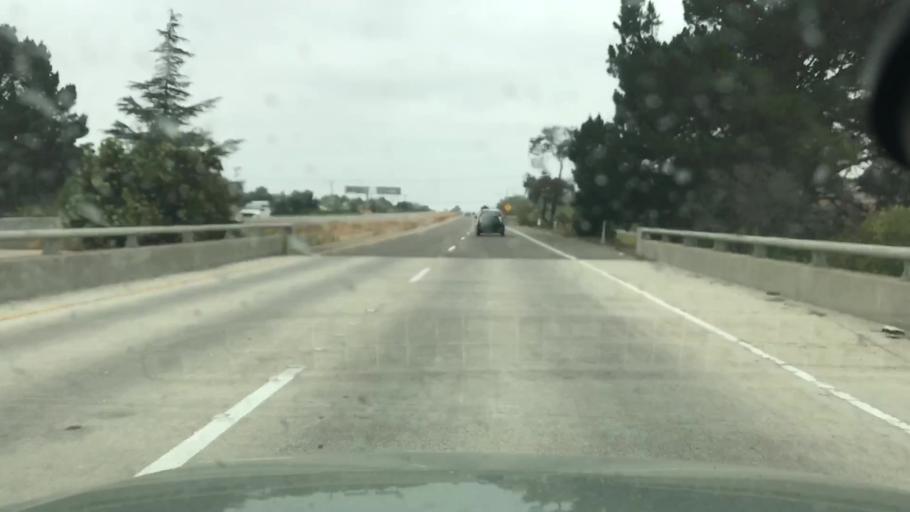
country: US
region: California
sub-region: Santa Barbara County
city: Orcutt
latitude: 34.8650
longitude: -120.4365
